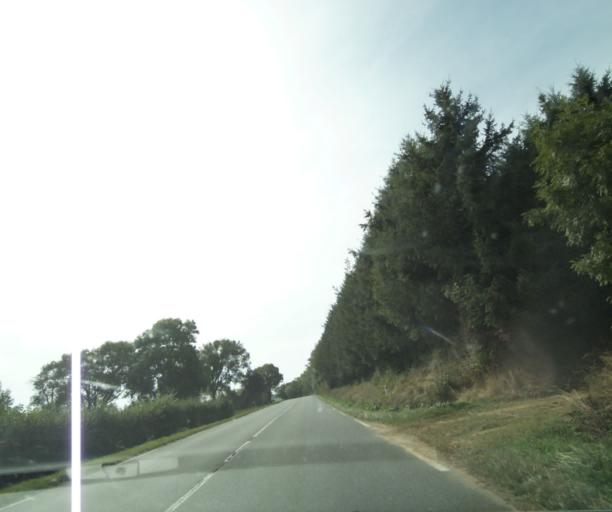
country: FR
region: Auvergne
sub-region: Departement de l'Allier
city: Le Donjon
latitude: 46.3245
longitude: 3.7664
